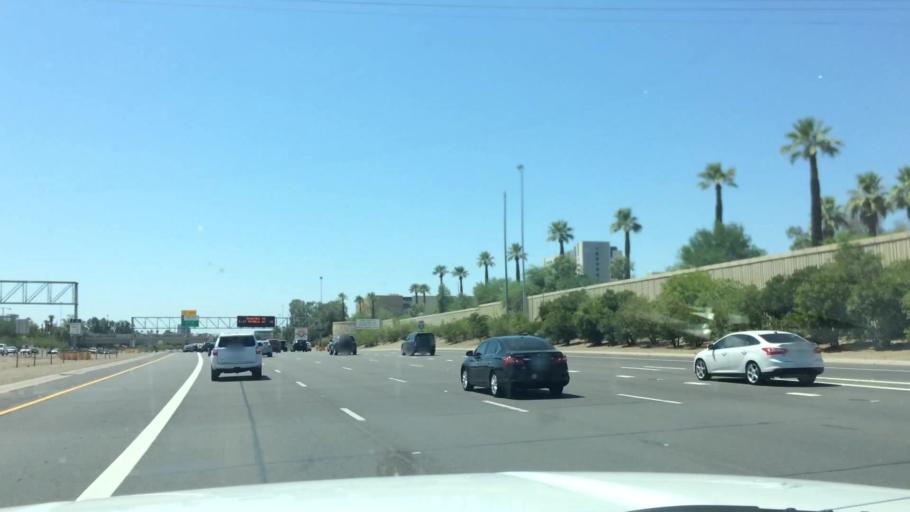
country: US
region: Arizona
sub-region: Maricopa County
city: Phoenix
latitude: 33.4604
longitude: -112.0516
